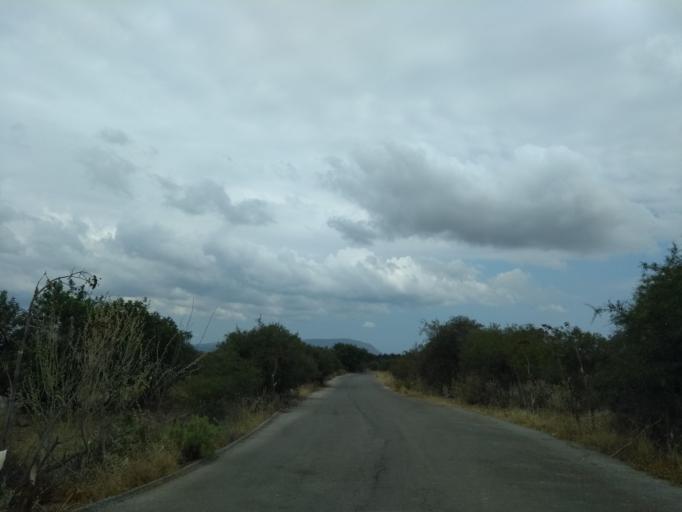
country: GR
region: Crete
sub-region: Nomos Chanias
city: Georgioupolis
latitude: 35.3958
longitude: 24.2304
